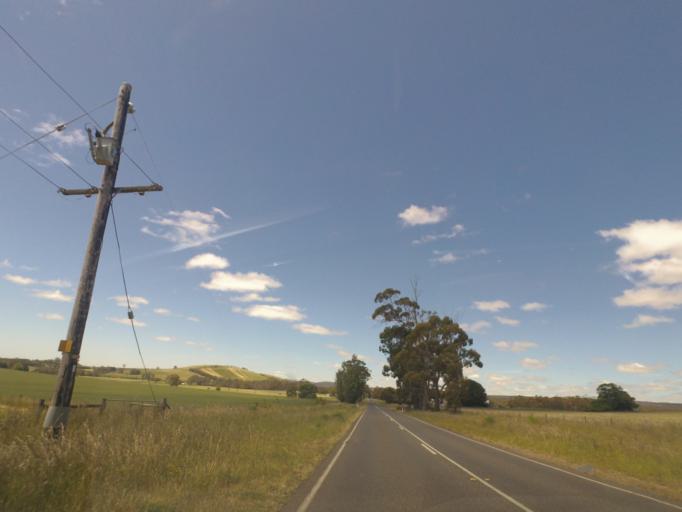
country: AU
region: Victoria
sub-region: Mount Alexander
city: Castlemaine
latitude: -37.3210
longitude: 144.2027
